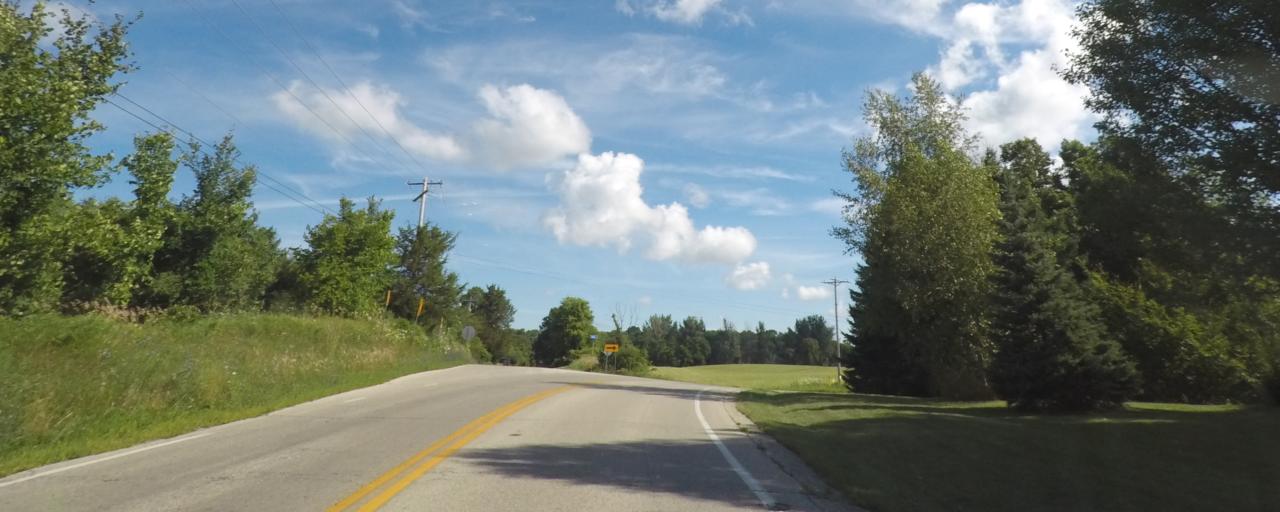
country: US
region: Wisconsin
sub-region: Waukesha County
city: Oconomowoc
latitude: 43.0801
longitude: -88.5400
